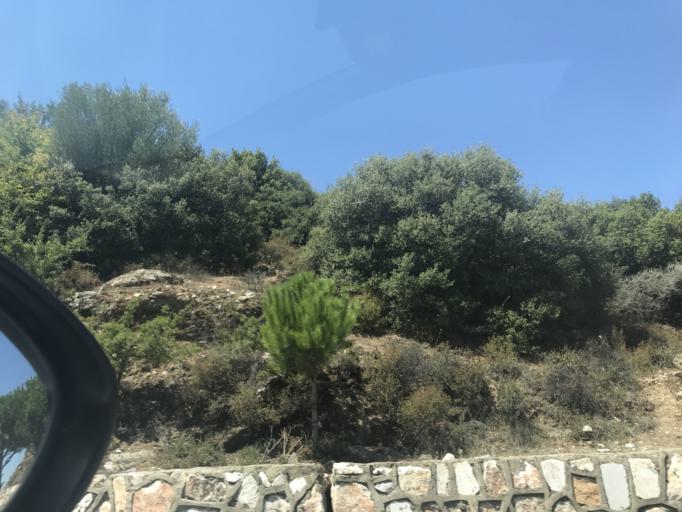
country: TR
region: Aydin
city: Akcaova
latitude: 37.4877
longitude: 28.1269
